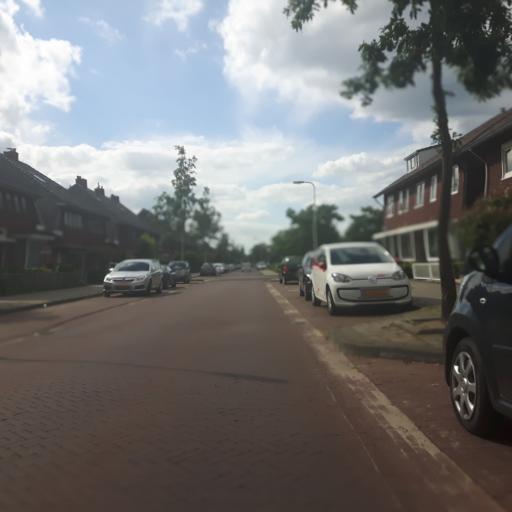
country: NL
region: Overijssel
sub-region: Gemeente Enschede
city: Enschede
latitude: 52.2127
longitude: 6.8684
